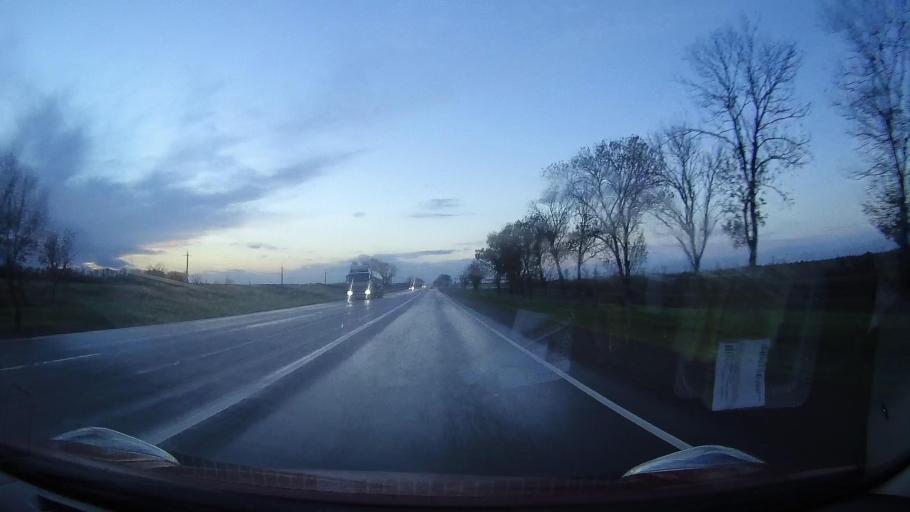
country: RU
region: Krasnodarskiy
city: Uspenskoye
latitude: 44.8139
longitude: 41.3800
